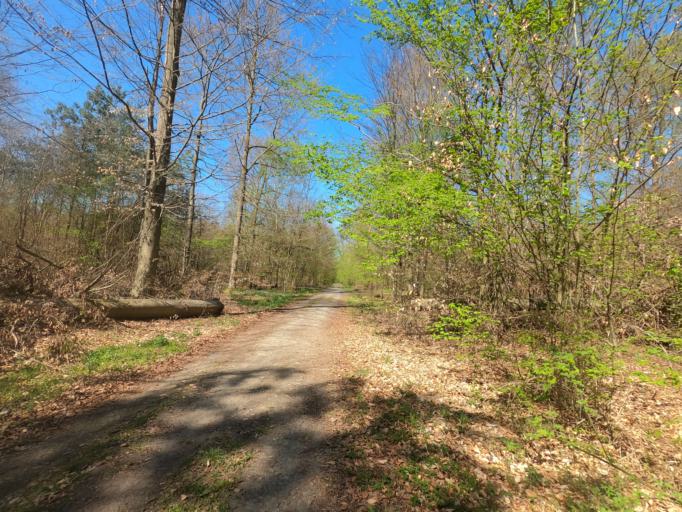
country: DE
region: Hesse
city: Morfelden-Walldorf
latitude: 49.9580
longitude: 8.5705
